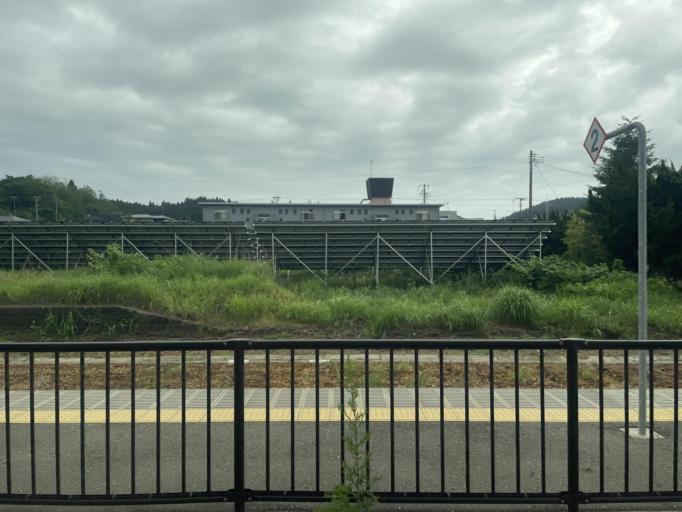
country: JP
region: Akita
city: Tenno
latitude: 39.9153
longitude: 139.9024
